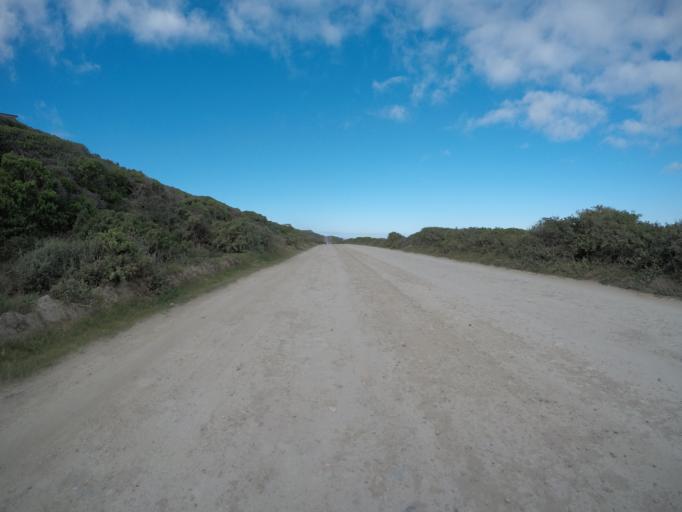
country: ZA
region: Western Cape
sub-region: Eden District Municipality
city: Riversdale
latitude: -34.4322
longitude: 21.3260
